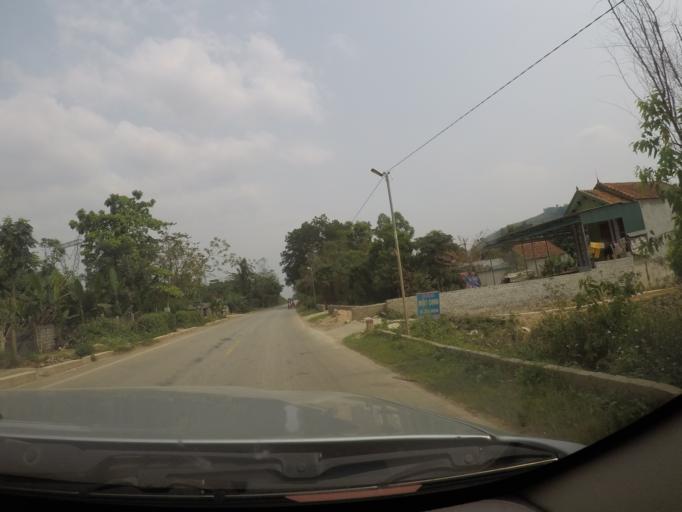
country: VN
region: Thanh Hoa
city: Thi Tran Yen Cat
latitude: 19.4778
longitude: 105.4127
